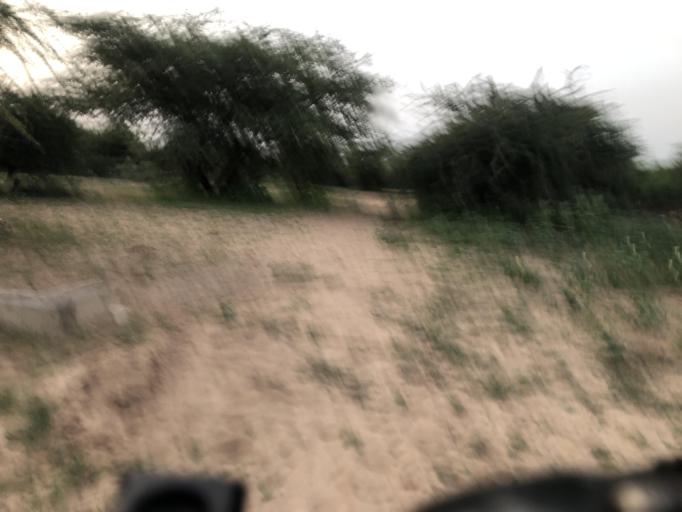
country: SN
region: Saint-Louis
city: Saint-Louis
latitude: 16.0618
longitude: -16.4326
